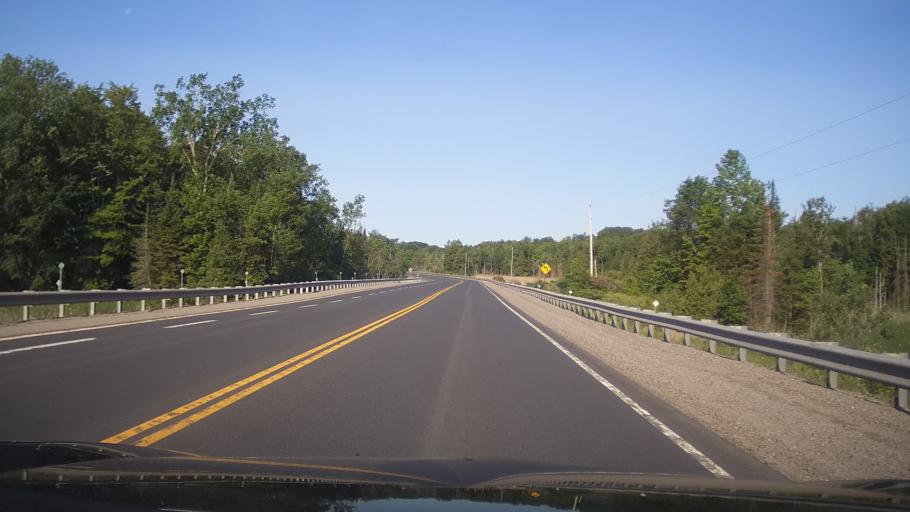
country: CA
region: Ontario
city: Belleville
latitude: 44.5383
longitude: -77.3749
